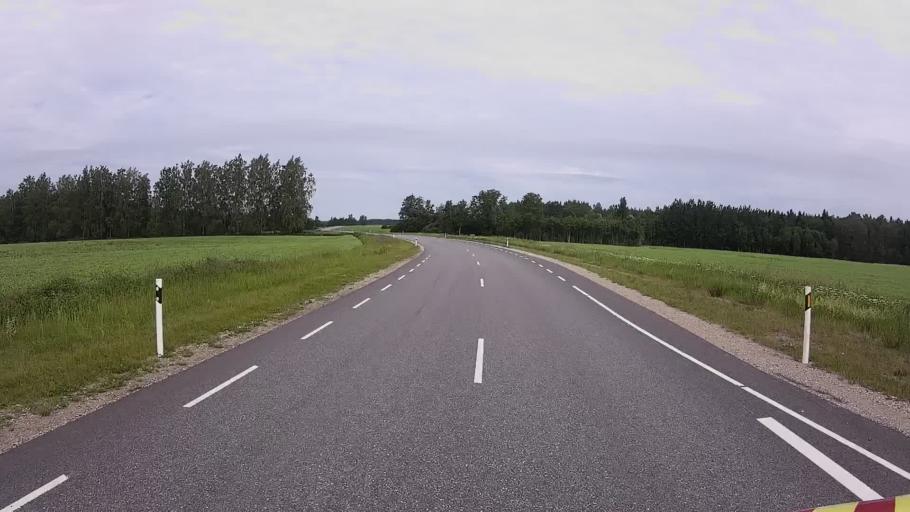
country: EE
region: Viljandimaa
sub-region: Karksi vald
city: Karksi-Nuia
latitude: 58.1579
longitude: 25.5933
